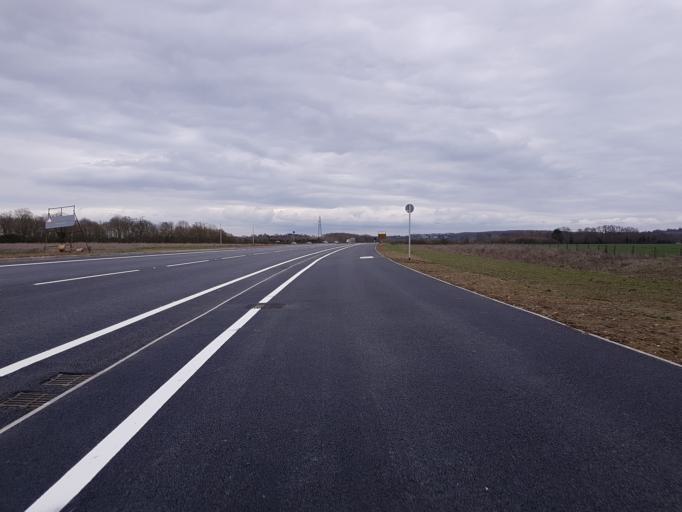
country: GB
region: England
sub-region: Cambridgeshire
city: Girton
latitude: 52.2436
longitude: 0.0425
